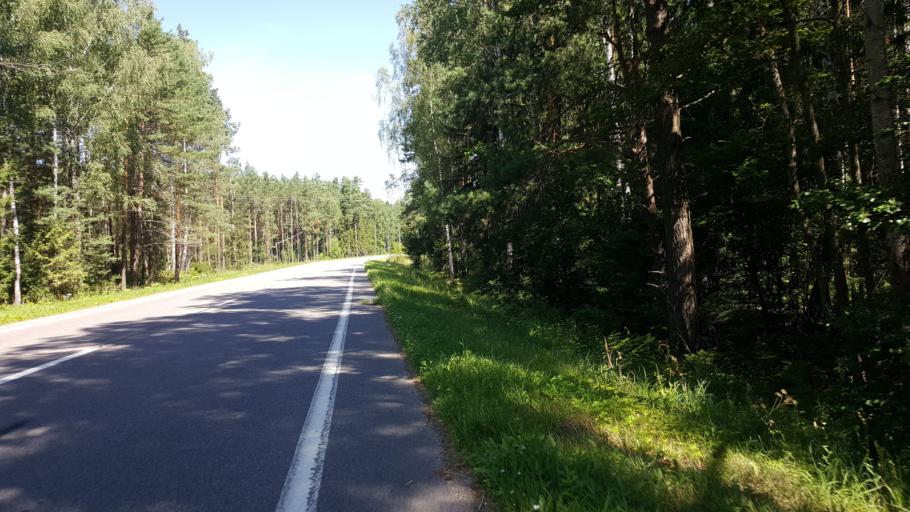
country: BY
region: Brest
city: Pruzhany
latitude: 52.4939
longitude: 24.1711
